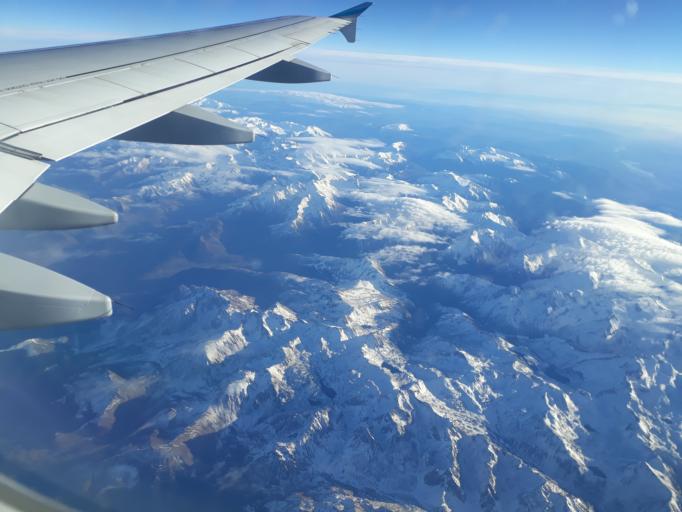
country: FR
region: Midi-Pyrenees
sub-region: Departement des Hautes-Pyrenees
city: Campan
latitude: 42.9875
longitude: 0.1148
